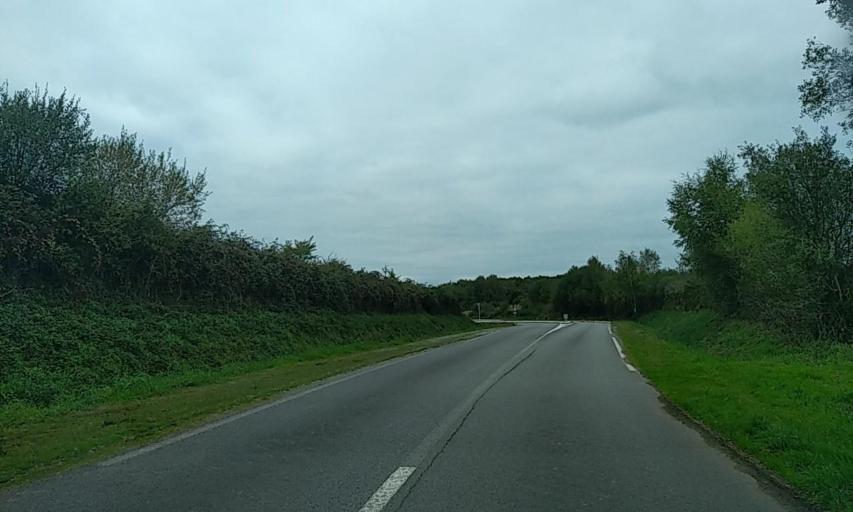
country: FR
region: Brittany
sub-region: Departement du Morbihan
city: Caudan
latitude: 47.8487
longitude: -3.3405
